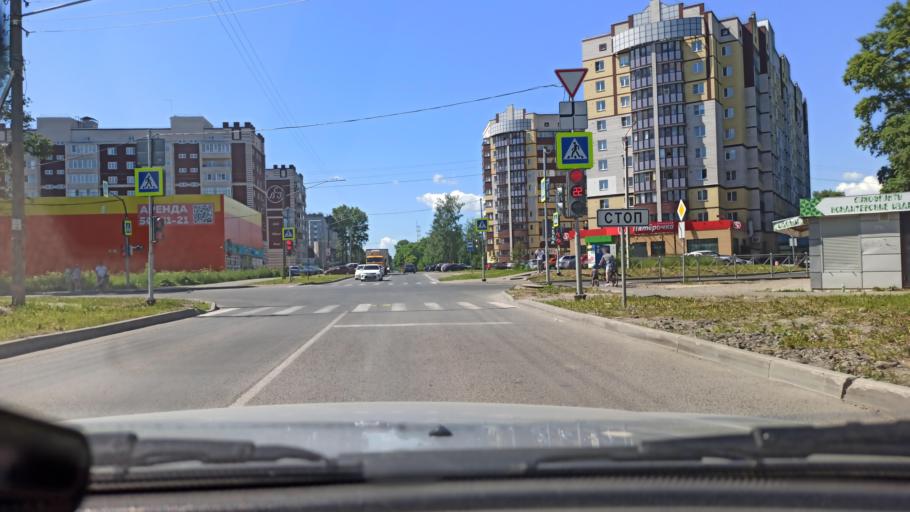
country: RU
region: Vologda
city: Vologda
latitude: 59.2175
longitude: 39.8504
